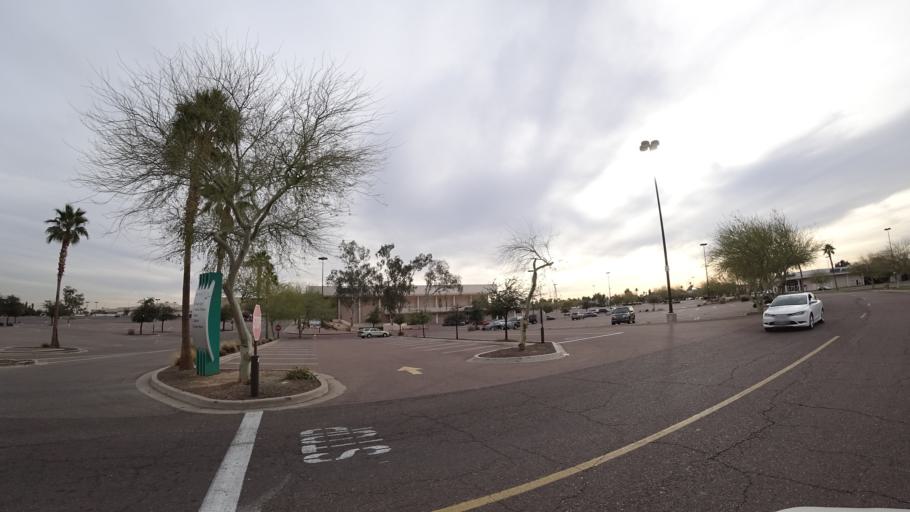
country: US
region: Arizona
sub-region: Maricopa County
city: Glendale
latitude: 33.5785
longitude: -112.1218
